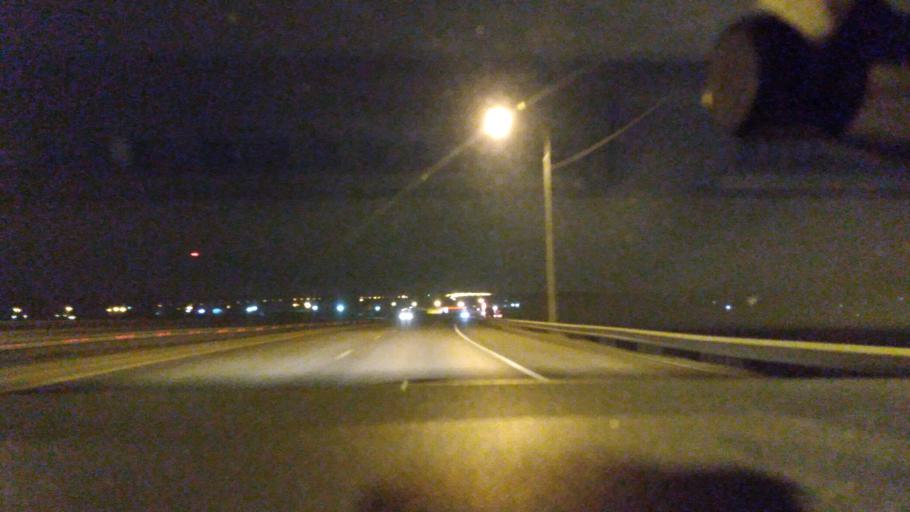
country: RU
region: Moskovskaya
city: Raduzhnyy
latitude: 55.1426
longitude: 38.7397
